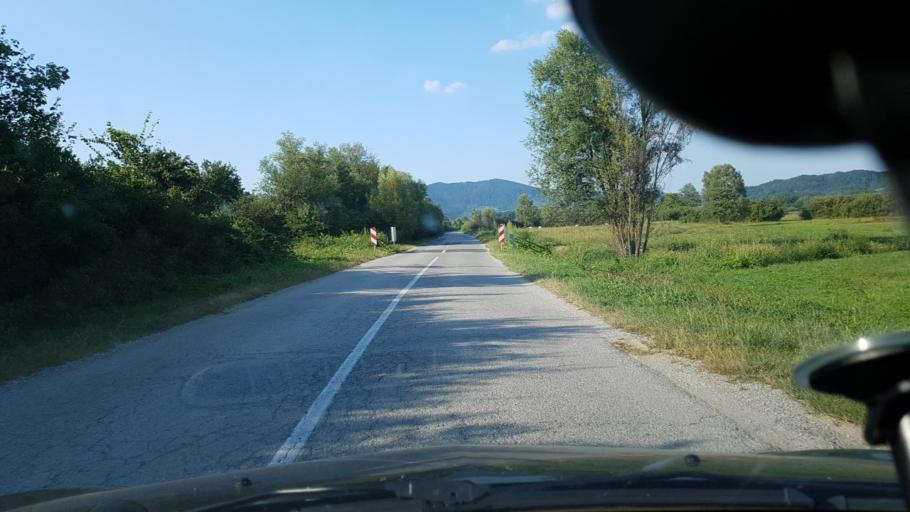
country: SI
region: Bistrica ob Sotli
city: Bistrica ob Sotli
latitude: 46.0114
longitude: 15.7157
